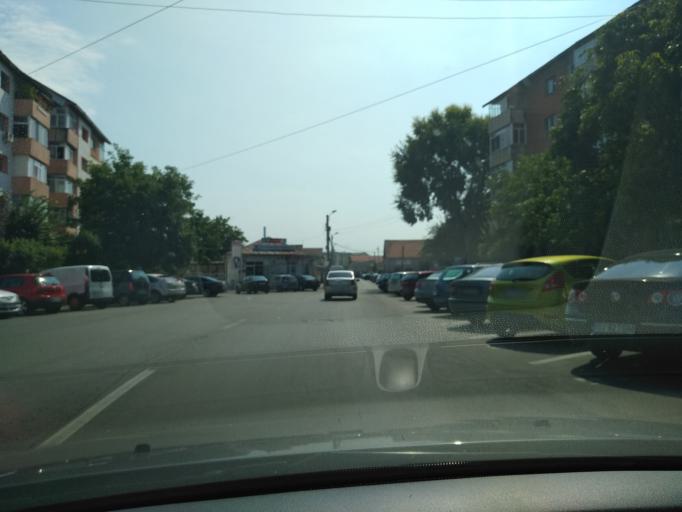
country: RO
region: Gorj
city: Targu Jiu
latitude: 45.0358
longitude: 23.2680
